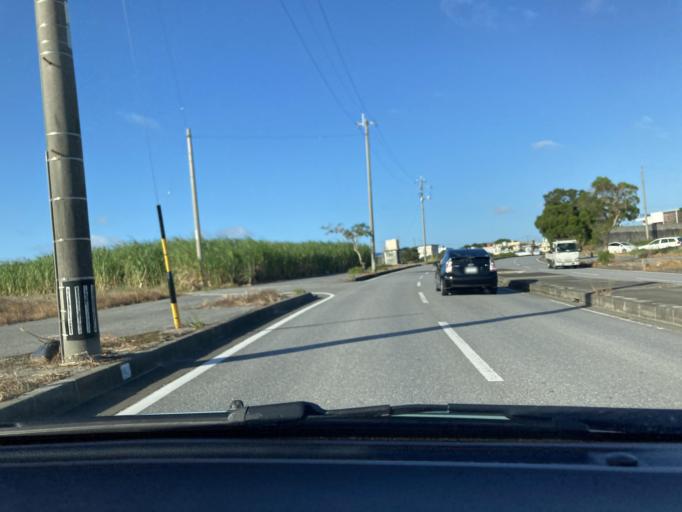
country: JP
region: Okinawa
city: Tomigusuku
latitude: 26.1614
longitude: 127.7028
